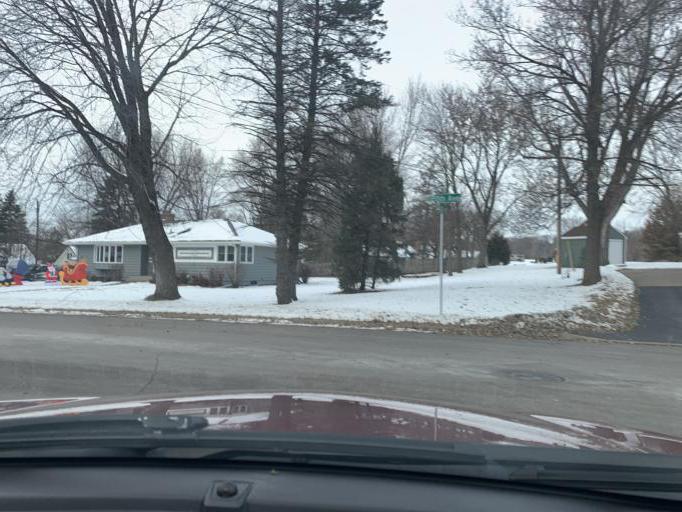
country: US
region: Minnesota
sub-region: Washington County
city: Saint Paul Park
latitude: 44.8440
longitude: -92.9855
